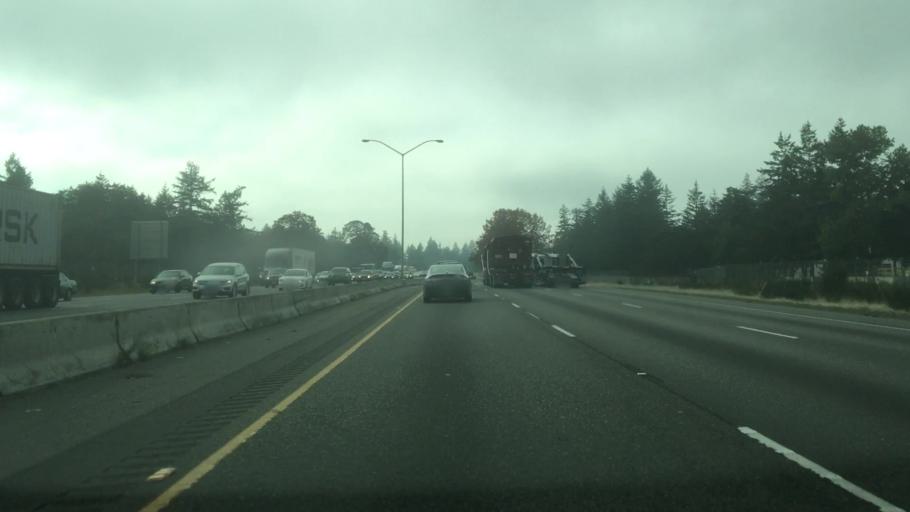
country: US
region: Washington
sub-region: Pierce County
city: Fort Lewis
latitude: 47.1146
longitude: -122.5641
